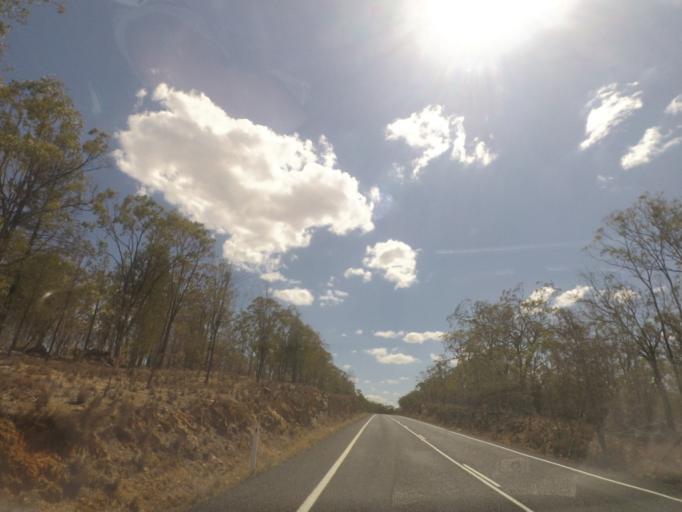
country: AU
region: Queensland
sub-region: Southern Downs
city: Warwick
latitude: -28.1620
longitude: 151.6849
